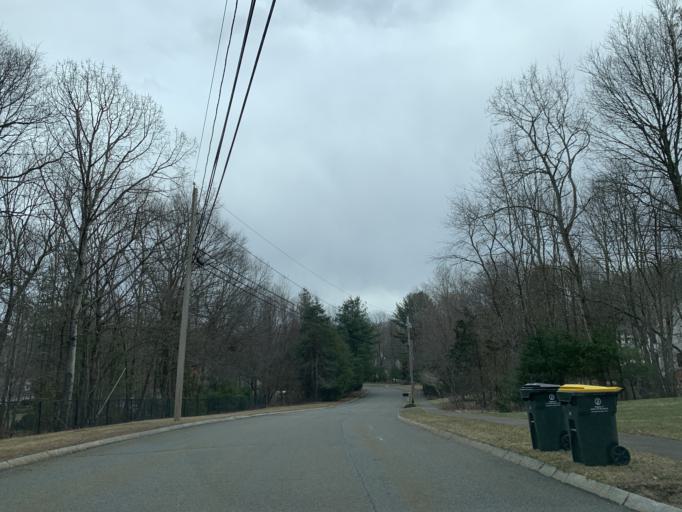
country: US
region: Massachusetts
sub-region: Norfolk County
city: Bellingham
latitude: 42.0457
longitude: -71.4476
